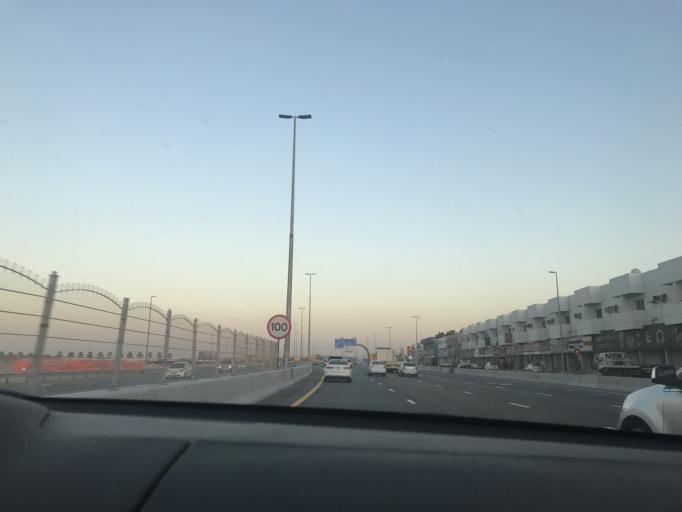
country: AE
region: Ash Shariqah
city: Sharjah
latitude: 25.1847
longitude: 55.3412
